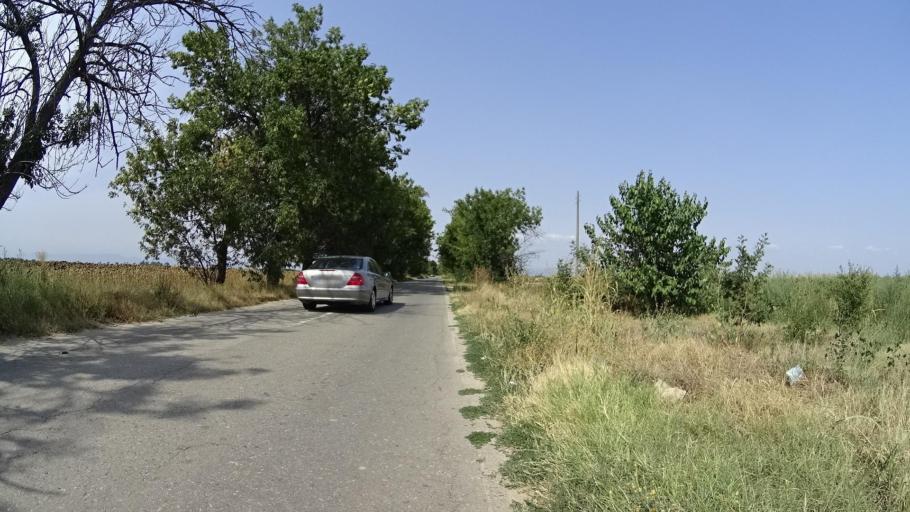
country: BG
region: Plovdiv
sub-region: Obshtina Plovdiv
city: Plovdiv
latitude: 42.2510
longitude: 24.7975
